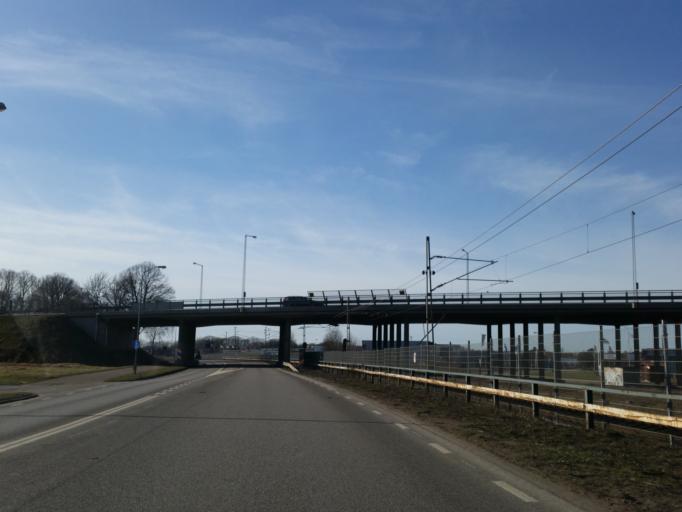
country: SE
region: Kalmar
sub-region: Kalmar Kommun
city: Kalmar
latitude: 56.6704
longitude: 16.3187
